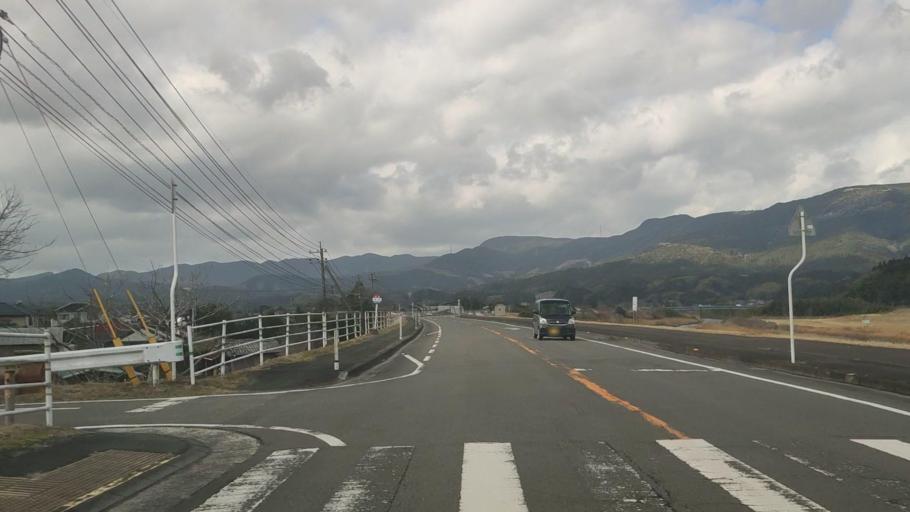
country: JP
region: Kumamoto
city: Hitoyoshi
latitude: 32.0553
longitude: 130.7969
